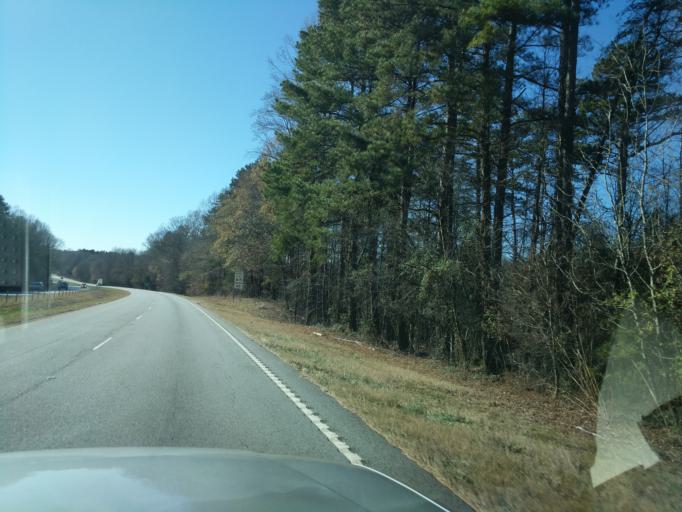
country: US
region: South Carolina
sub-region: Pickens County
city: Liberty
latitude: 34.7848
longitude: -82.6657
